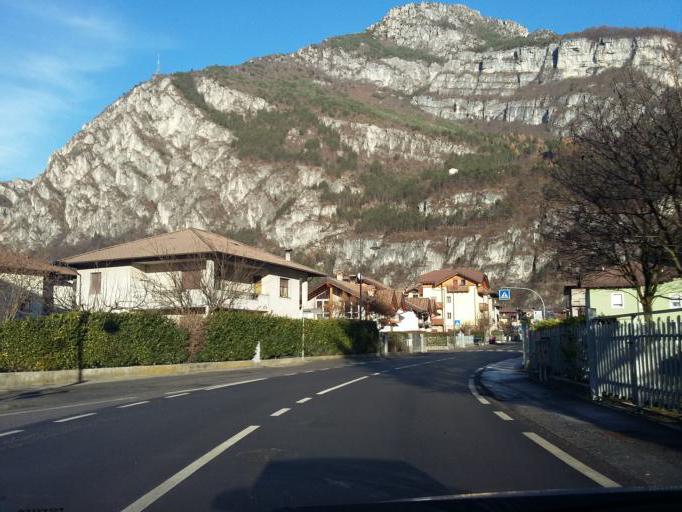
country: IT
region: Trentino-Alto Adige
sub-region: Provincia di Trento
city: Storo
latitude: 45.8467
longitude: 10.5751
